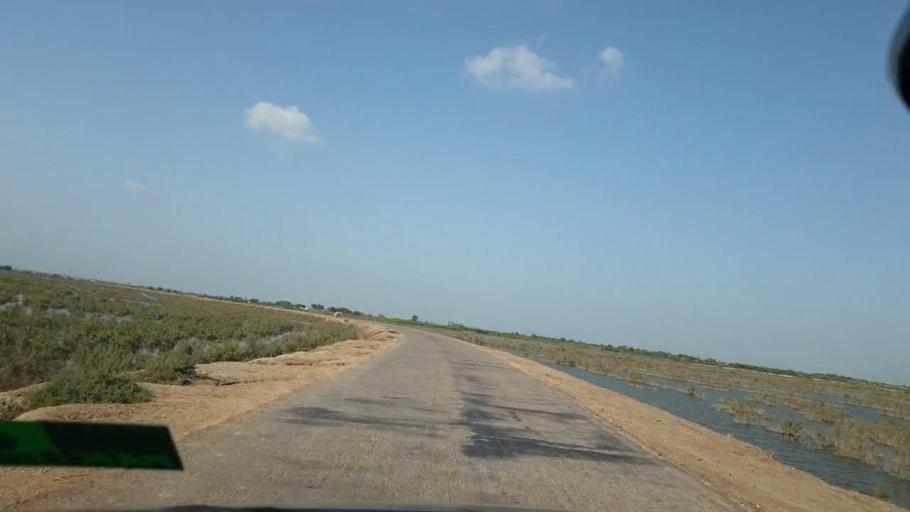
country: PK
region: Sindh
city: Tando Bago
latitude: 24.7275
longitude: 69.1982
